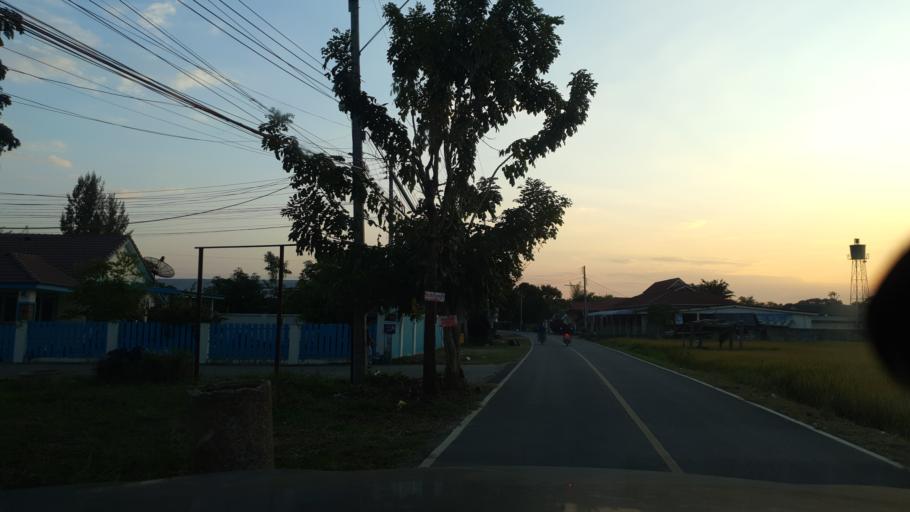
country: TH
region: Chiang Mai
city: San Sai
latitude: 18.8507
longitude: 99.0728
